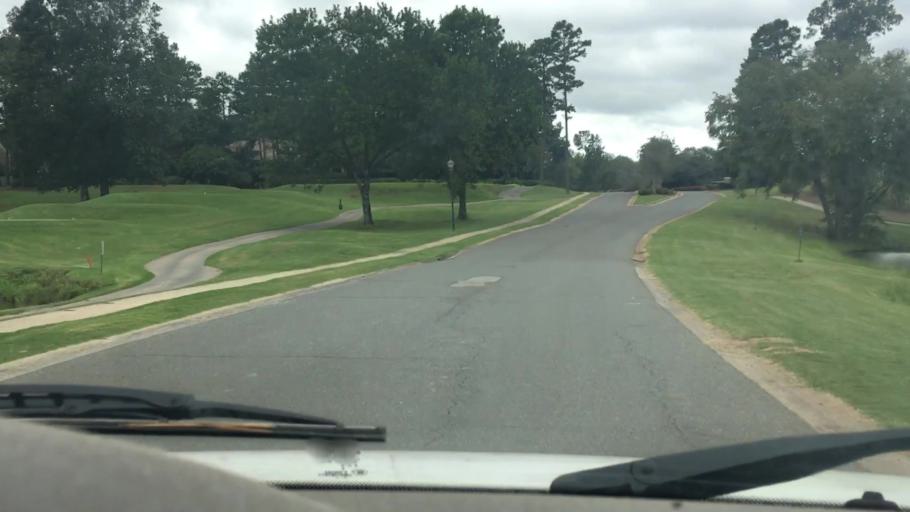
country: US
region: North Carolina
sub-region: Gaston County
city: Davidson
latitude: 35.4649
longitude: -80.8025
